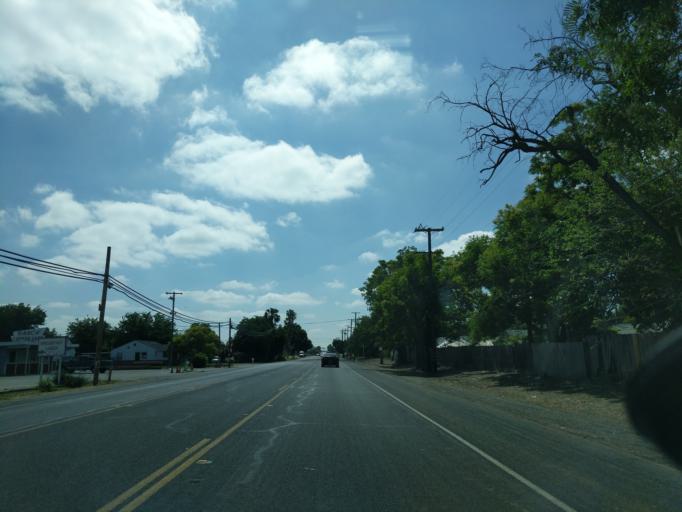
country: US
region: California
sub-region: San Joaquin County
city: Kennedy
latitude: 37.9407
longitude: -121.2477
